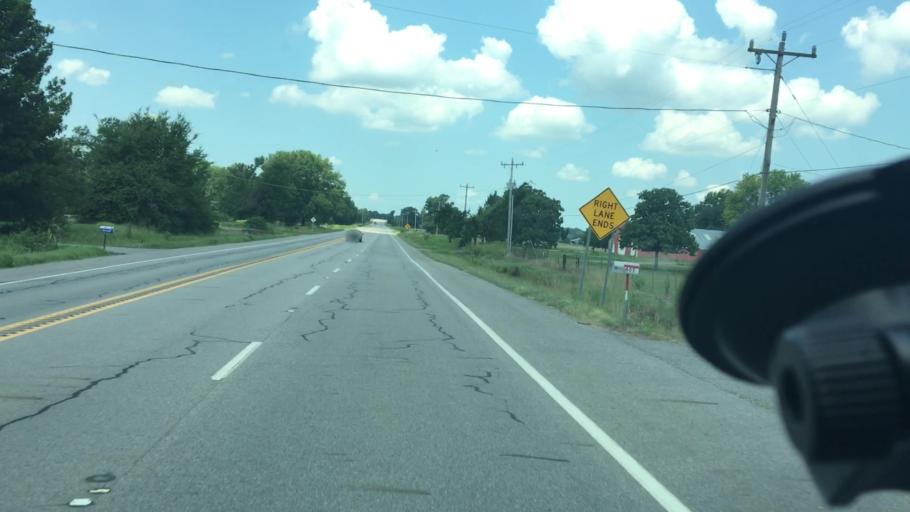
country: US
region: Arkansas
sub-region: Logan County
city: Paris
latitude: 35.2985
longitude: -93.8136
